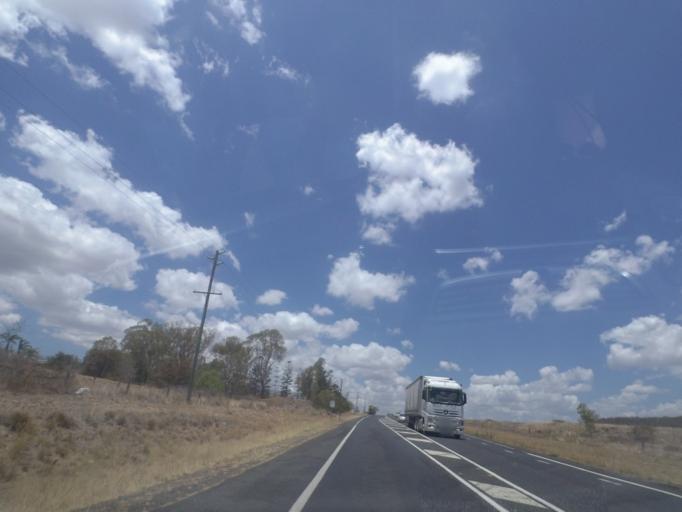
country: AU
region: Queensland
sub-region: Toowoomba
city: Top Camp
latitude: -27.7295
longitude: 151.9120
